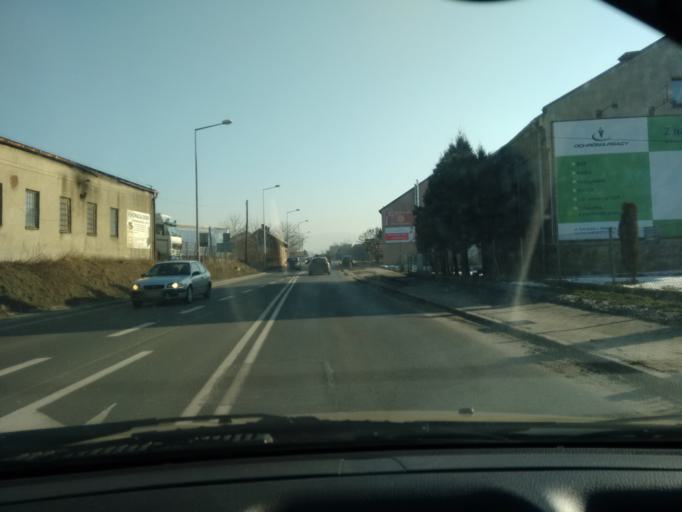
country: PL
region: Lesser Poland Voivodeship
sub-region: Powiat wadowicki
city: Wadowice
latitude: 49.8860
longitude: 19.5001
